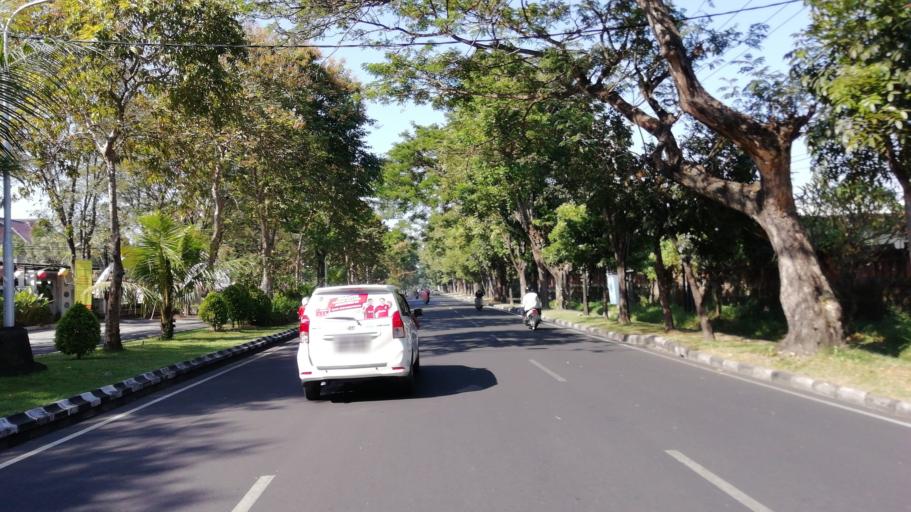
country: ID
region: Bali
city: Banjar Batanpoh
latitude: -8.6684
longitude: 115.2385
